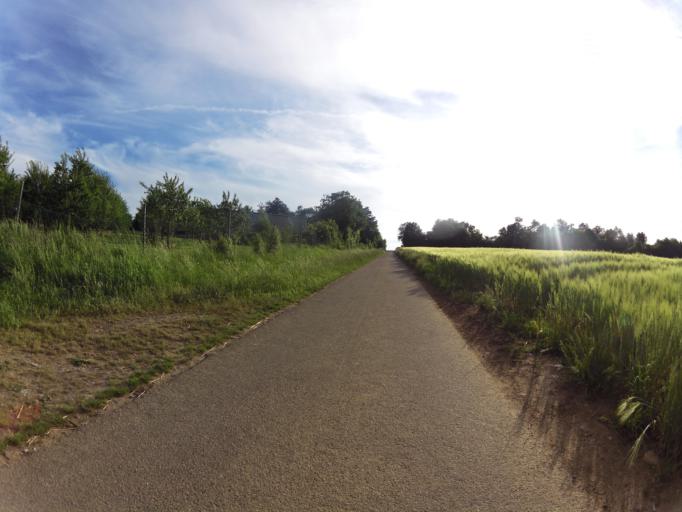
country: DE
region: Bavaria
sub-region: Regierungsbezirk Unterfranken
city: Sommerhausen
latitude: 49.6983
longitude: 10.0420
